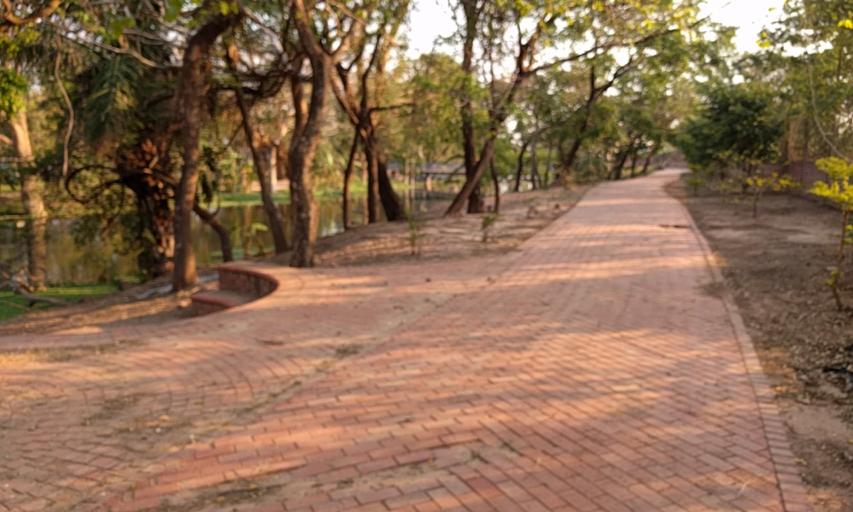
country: BO
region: Santa Cruz
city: Warnes
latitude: -17.4476
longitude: -63.1858
